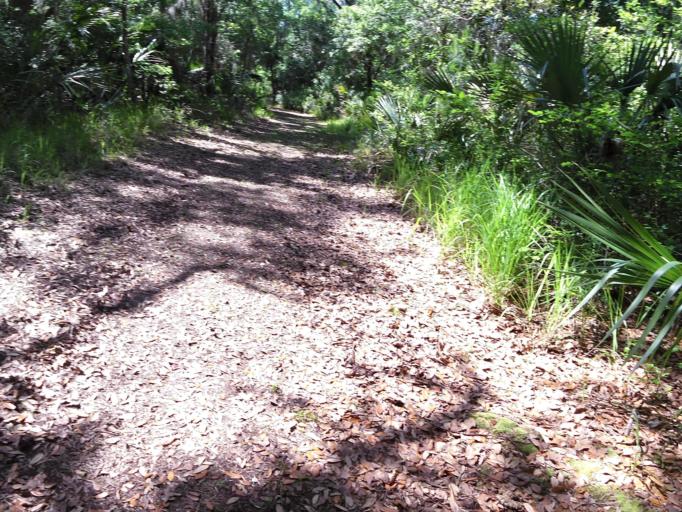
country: US
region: Florida
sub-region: Duval County
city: Atlantic Beach
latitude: 30.4444
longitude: -81.4797
